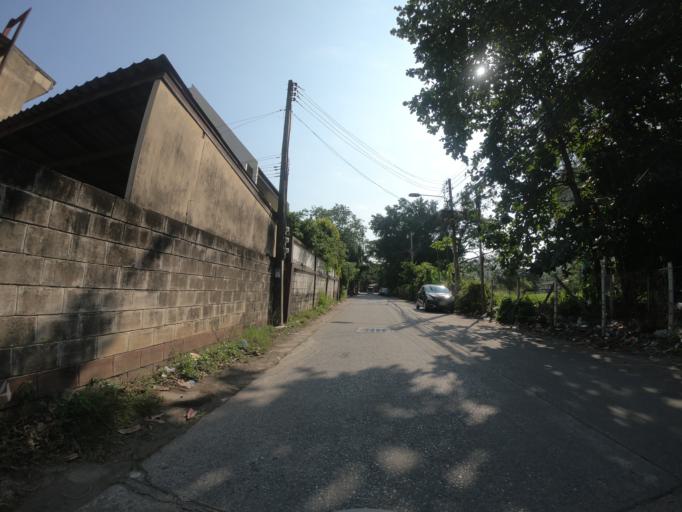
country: TH
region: Chiang Mai
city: Chiang Mai
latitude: 18.7982
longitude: 98.9782
